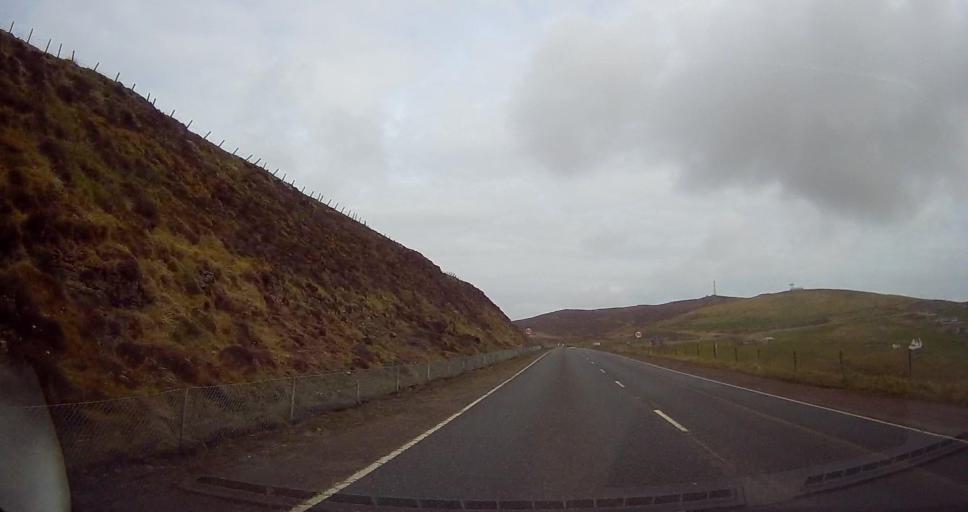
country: GB
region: Scotland
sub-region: Shetland Islands
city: Lerwick
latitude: 60.1337
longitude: -1.2141
